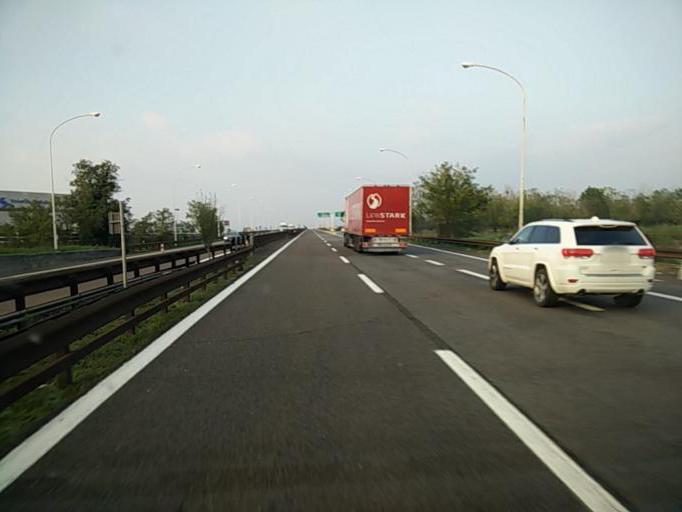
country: IT
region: Veneto
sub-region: Provincia di Verona
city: Dossobuono
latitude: 45.4012
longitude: 10.9110
